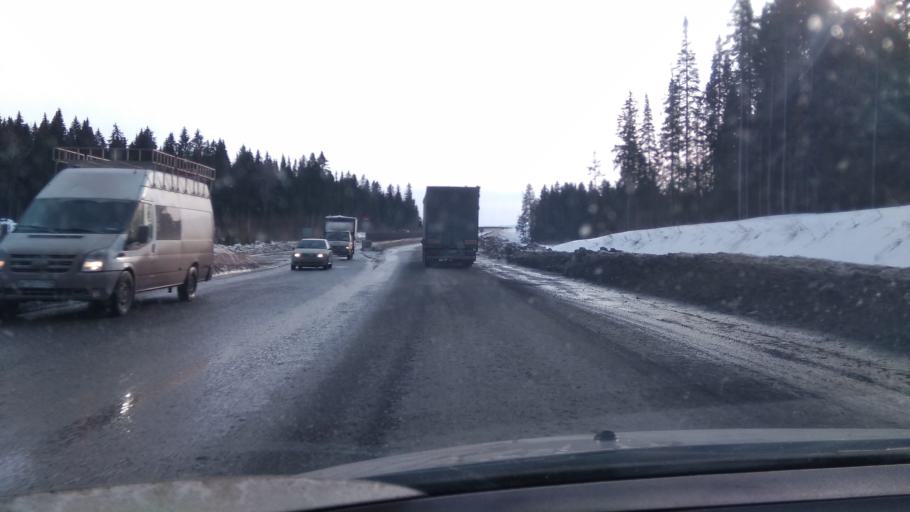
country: RU
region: Perm
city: Ferma
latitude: 57.9464
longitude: 56.3838
